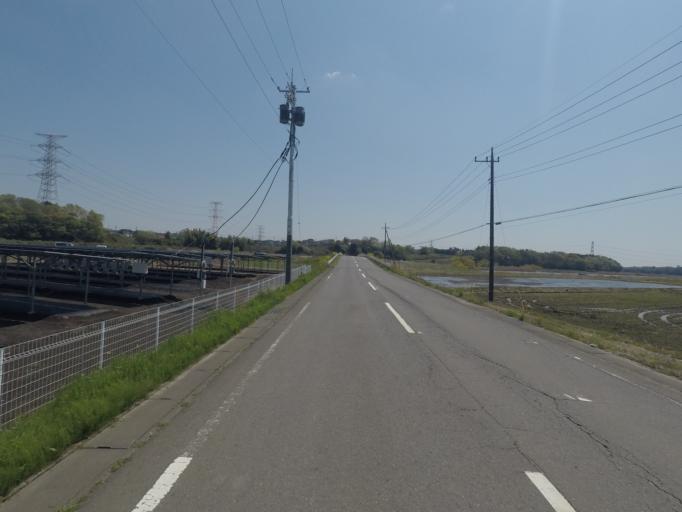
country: JP
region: Ibaraki
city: Ushiku
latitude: 36.0092
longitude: 140.0967
